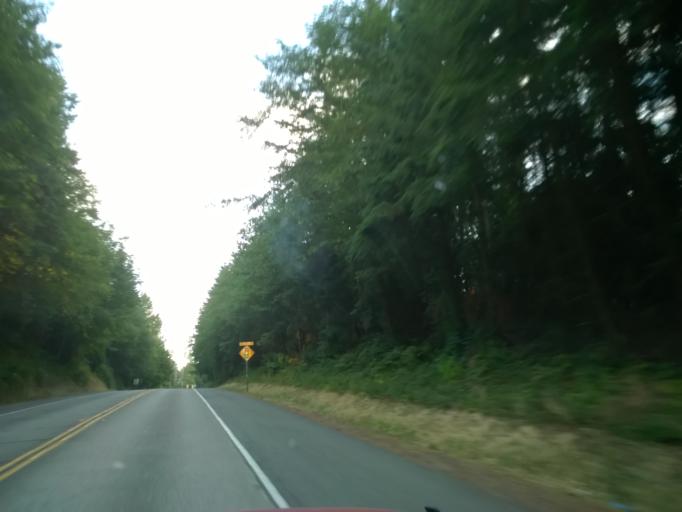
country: US
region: Washington
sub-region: King County
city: Redmond
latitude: 47.7140
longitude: -122.1127
